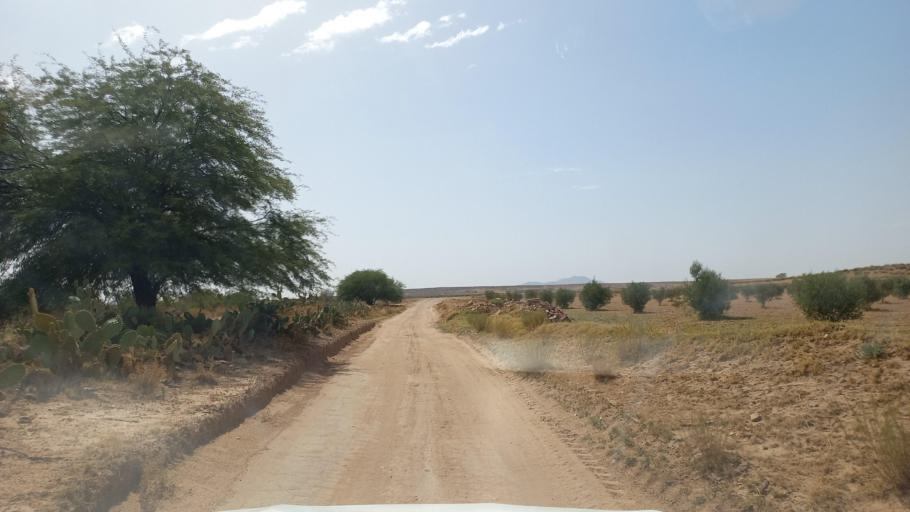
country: TN
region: Al Qasrayn
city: Kasserine
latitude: 35.2547
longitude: 8.9590
